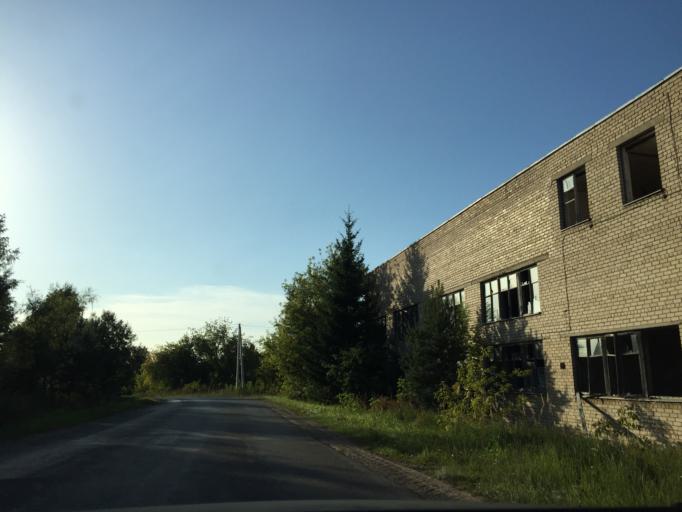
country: LT
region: Panevezys
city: Rokiskis
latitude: 55.9075
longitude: 25.6403
